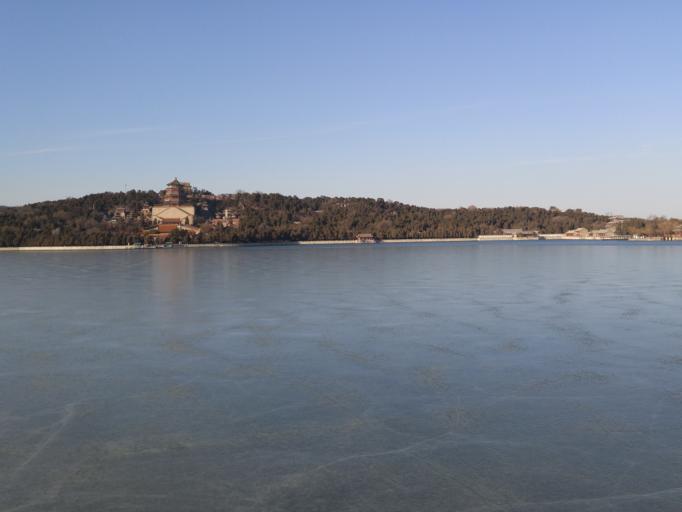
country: CN
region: Beijing
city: Haidian
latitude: 39.9906
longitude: 116.2700
